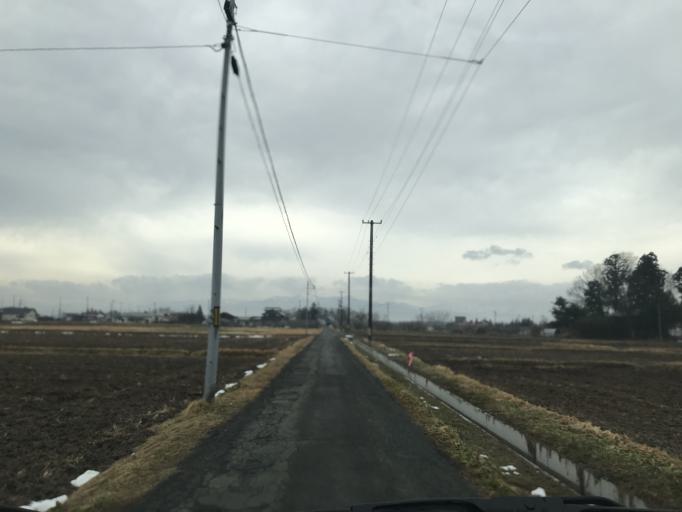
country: JP
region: Iwate
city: Mizusawa
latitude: 39.1835
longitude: 141.1338
